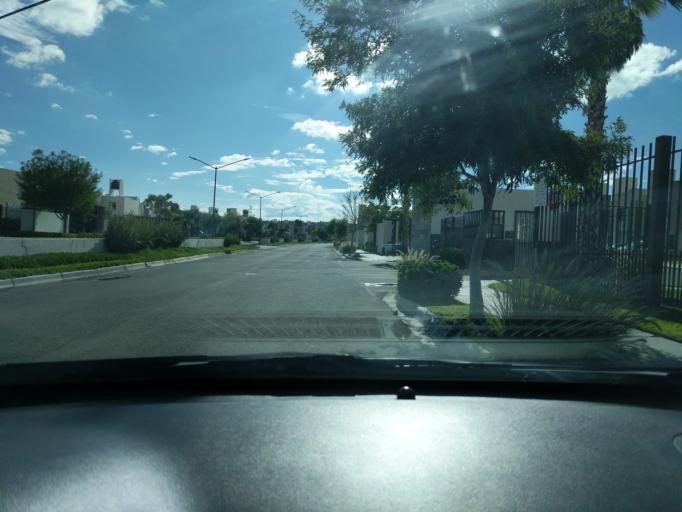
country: MX
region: Queretaro
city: El Colorado
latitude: 20.5846
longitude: -100.2825
